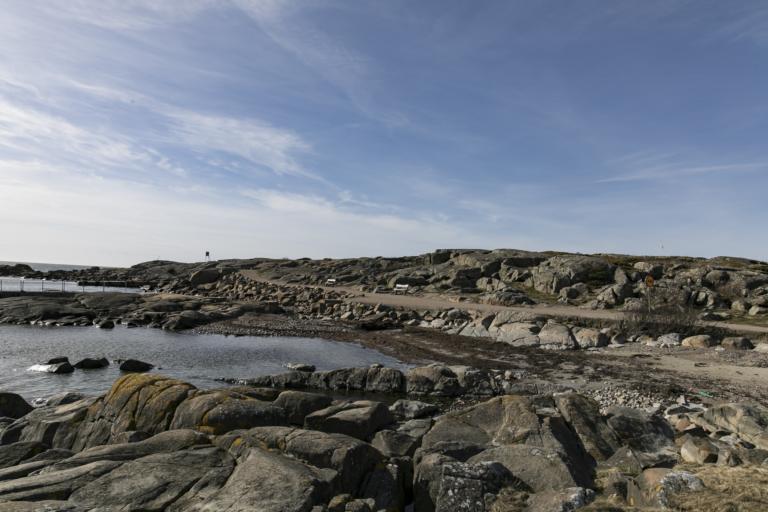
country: SE
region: Halland
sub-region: Varbergs Kommun
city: Varberg
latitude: 57.1148
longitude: 12.2120
